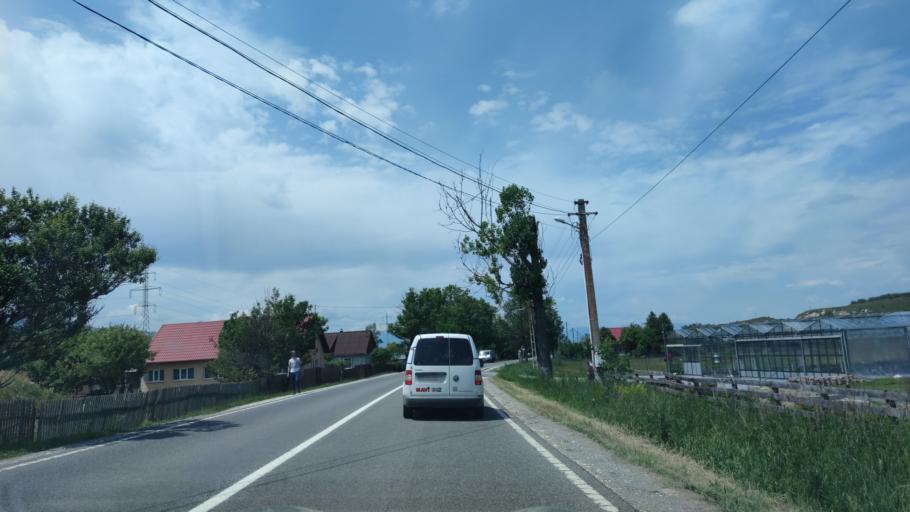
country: RO
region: Harghita
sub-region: Comuna Voslobeni
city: Voslobeni
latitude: 46.6243
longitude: 25.6359
